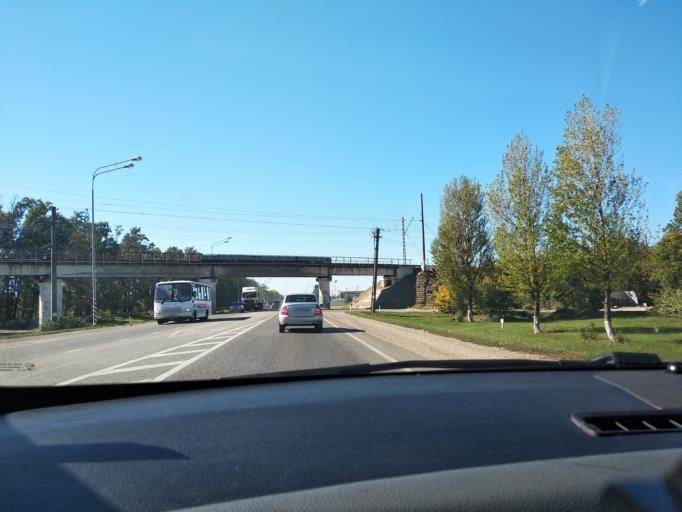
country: RU
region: Krasnodarskiy
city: Krasnodar
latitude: 45.1366
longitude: 39.0309
